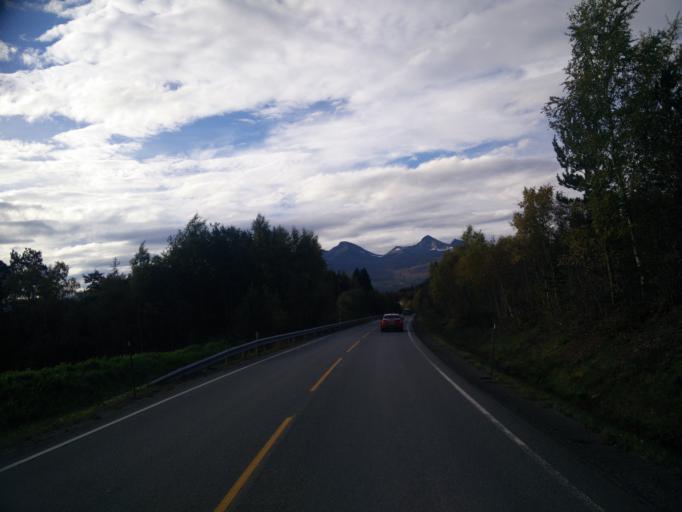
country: NO
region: More og Romsdal
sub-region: Vestnes
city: Vestnes
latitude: 62.6415
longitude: 7.0811
